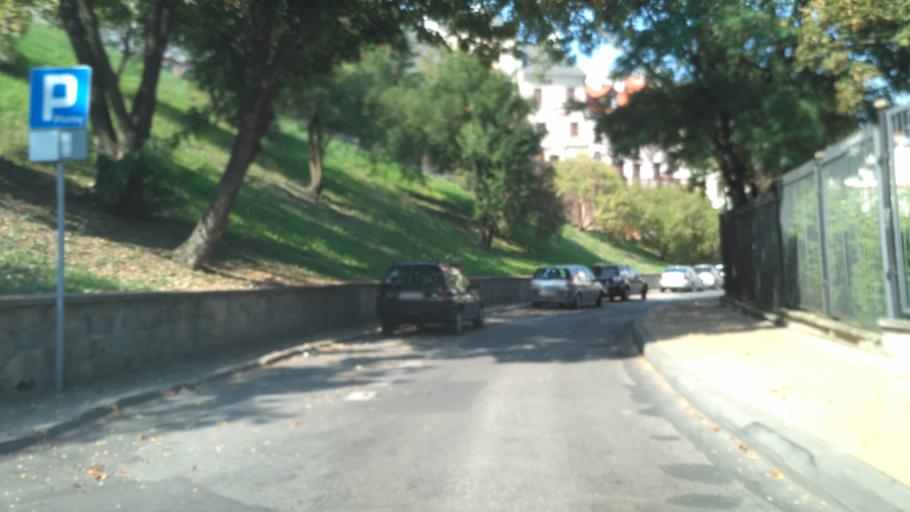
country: PL
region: Lublin Voivodeship
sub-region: Powiat lubelski
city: Lublin
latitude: 51.2487
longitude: 22.5702
